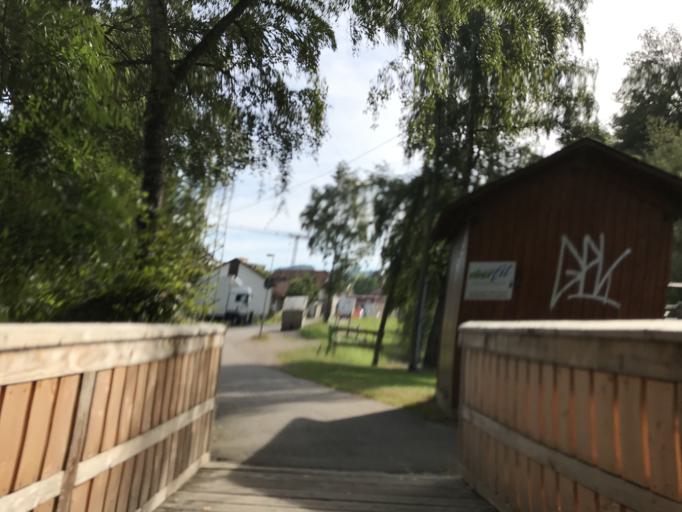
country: DE
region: Baden-Wuerttemberg
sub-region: Freiburg Region
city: Schopfheim
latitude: 47.6561
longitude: 7.8283
